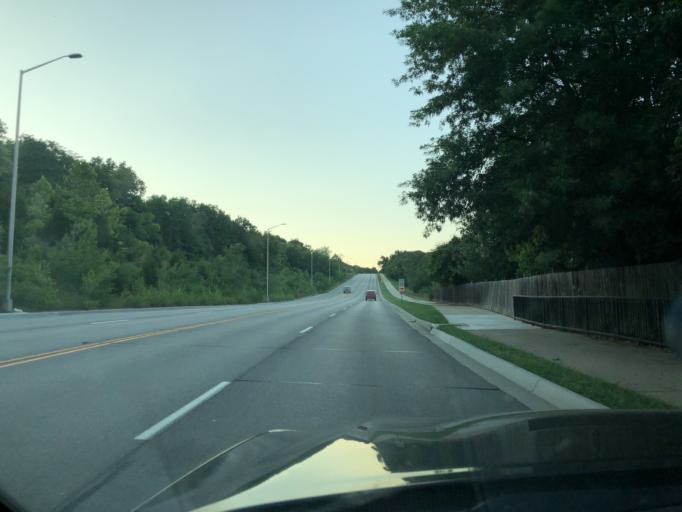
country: US
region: Kansas
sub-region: Leavenworth County
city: Leavenworth
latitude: 39.2938
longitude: -94.9502
